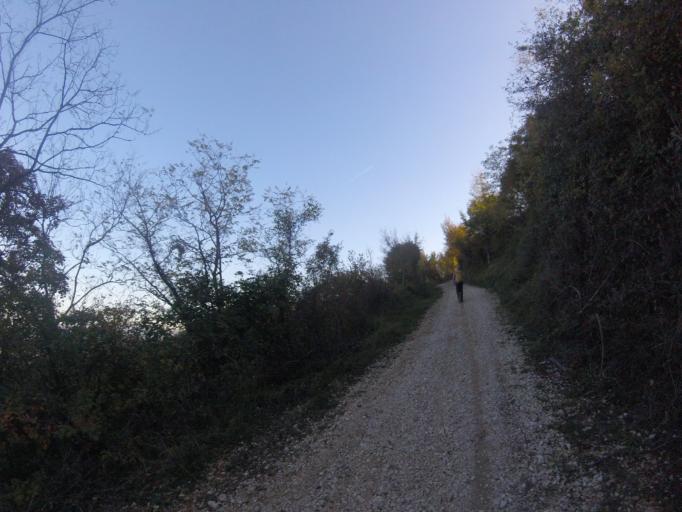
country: HR
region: Istarska
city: Pazin
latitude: 45.2232
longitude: 14.0066
